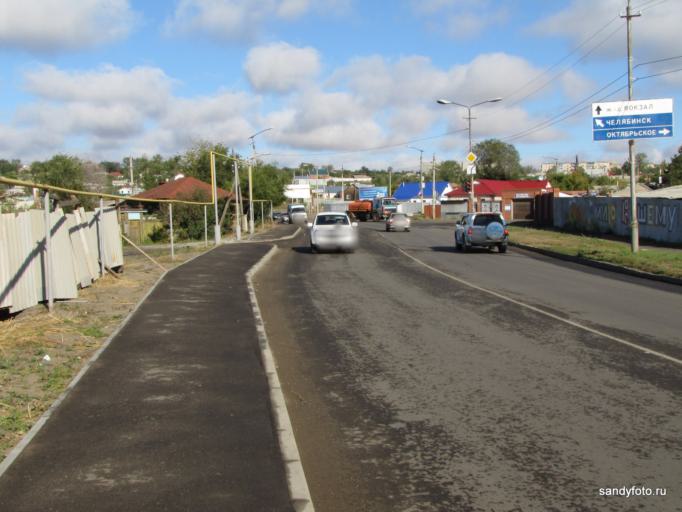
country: RU
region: Chelyabinsk
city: Troitsk
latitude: 54.0962
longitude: 61.5638
